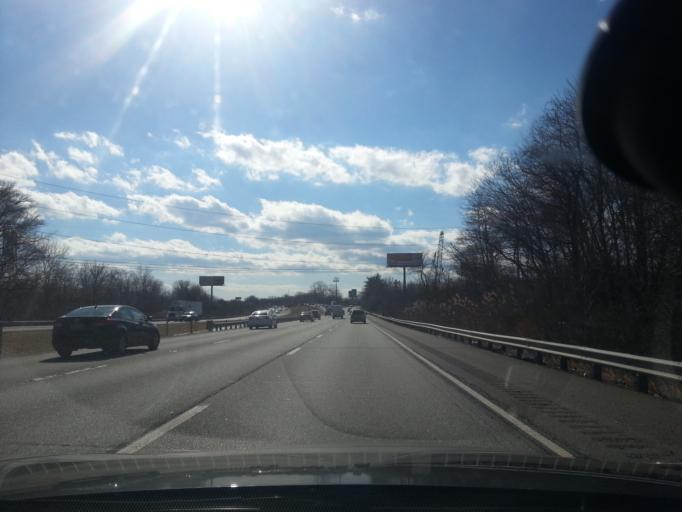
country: US
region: Pennsylvania
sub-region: Delaware County
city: Trainer
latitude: 39.8362
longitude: -75.4188
